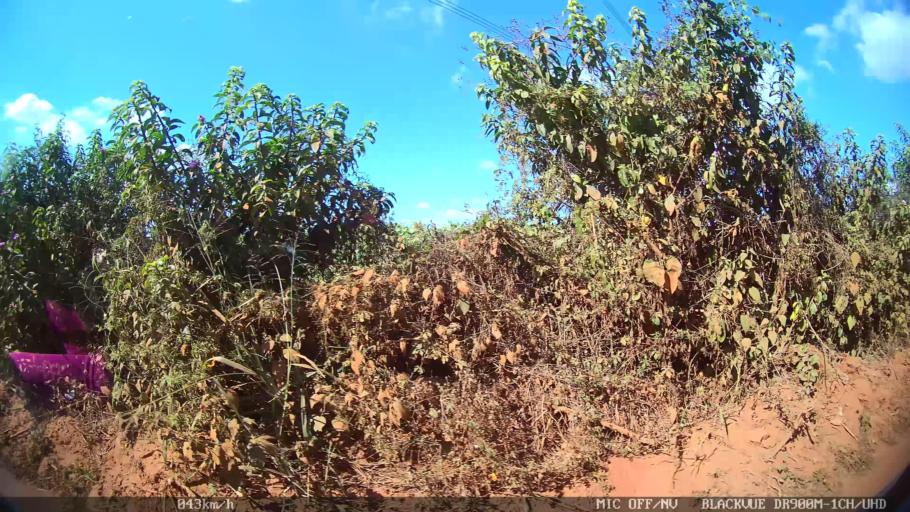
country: BR
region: Sao Paulo
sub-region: Sumare
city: Sumare
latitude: -22.8555
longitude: -47.2934
